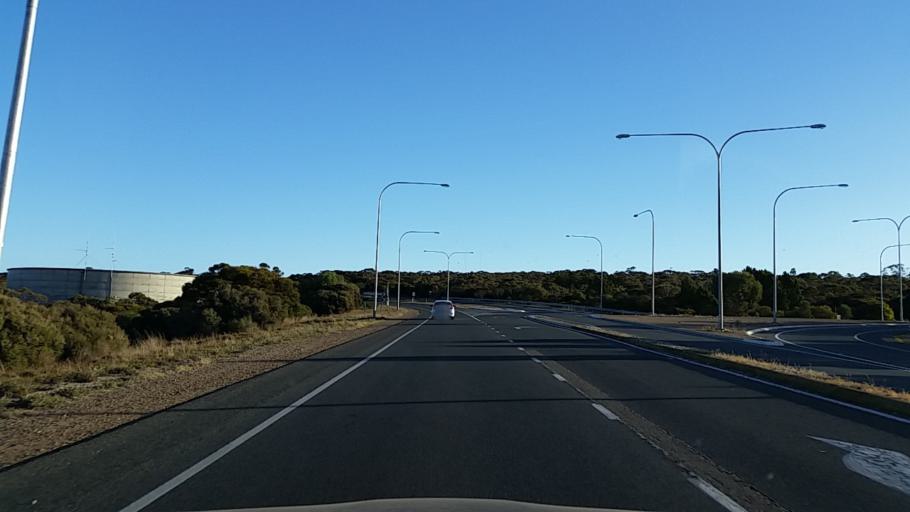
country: AU
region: South Australia
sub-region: Murray Bridge
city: Murray Bridge
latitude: -35.1398
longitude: 139.2288
